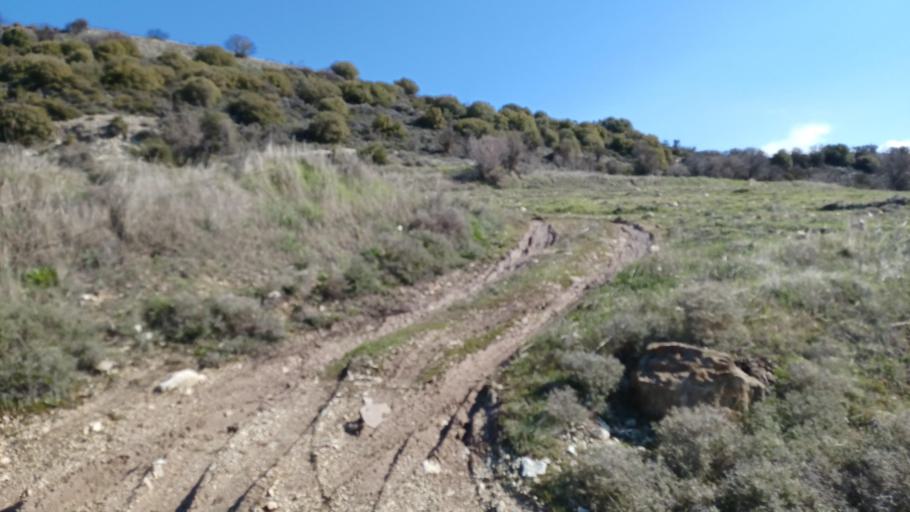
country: CY
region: Limassol
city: Pachna
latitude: 34.8236
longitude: 32.6872
